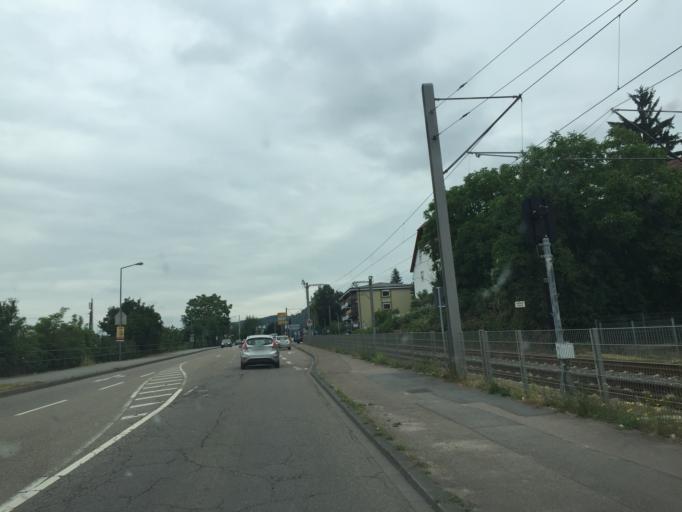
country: DE
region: Baden-Wuerttemberg
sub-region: Karlsruhe Region
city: Weinheim
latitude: 49.5502
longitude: 8.6651
